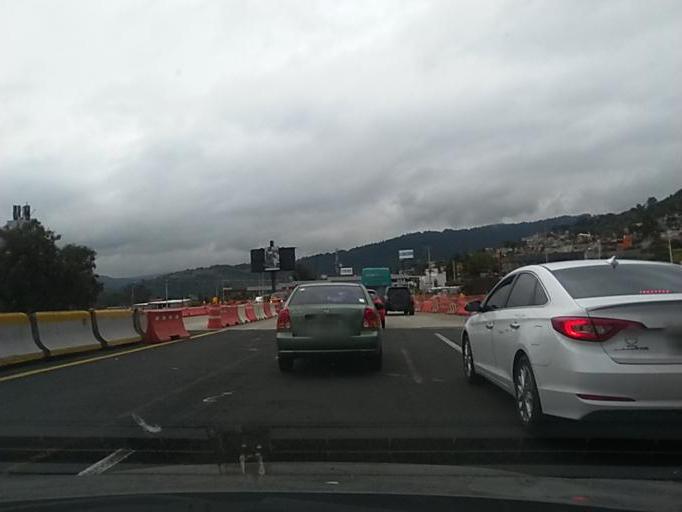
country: MX
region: Mexico City
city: Xochimilco
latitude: 19.2439
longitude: -99.1495
